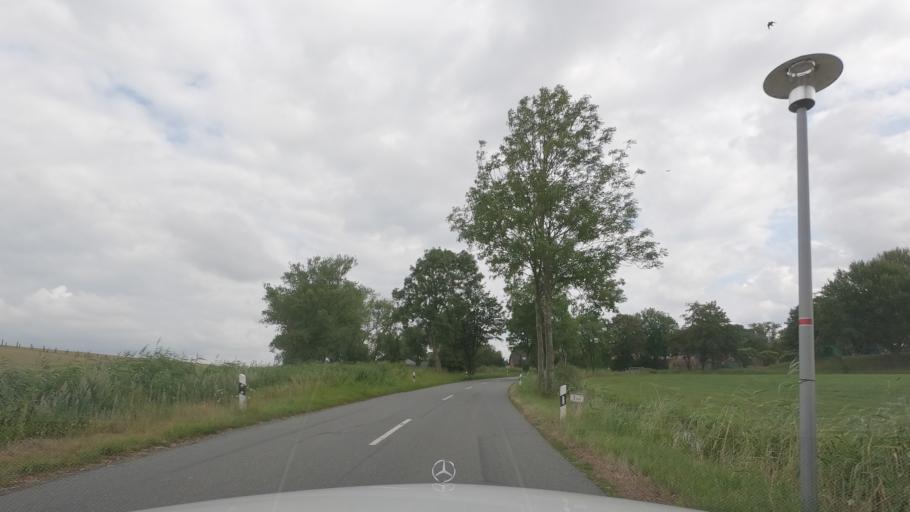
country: DE
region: Lower Saxony
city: Brake (Unterweser)
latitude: 53.3085
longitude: 8.5296
